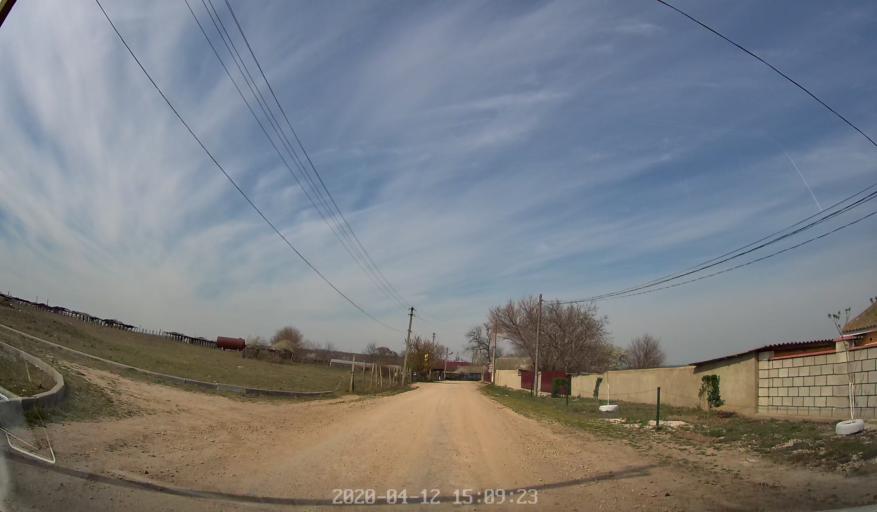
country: MD
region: Telenesti
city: Cocieri
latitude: 47.3200
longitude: 29.0688
